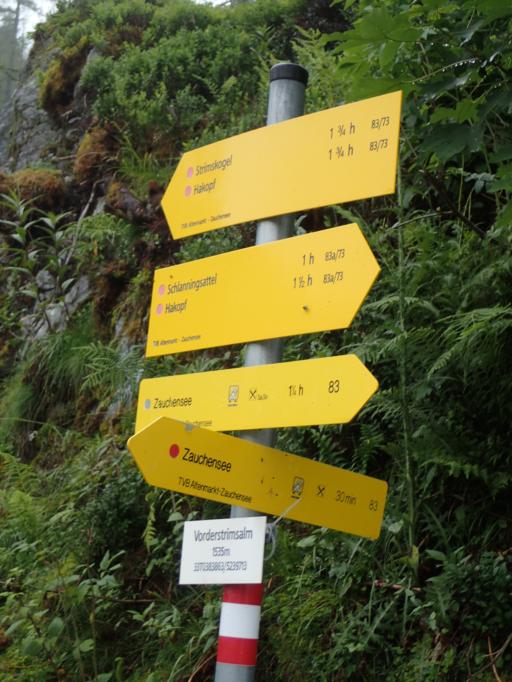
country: AT
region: Salzburg
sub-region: Politischer Bezirk Sankt Johann im Pongau
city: Untertauern
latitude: 47.3005
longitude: 13.4638
